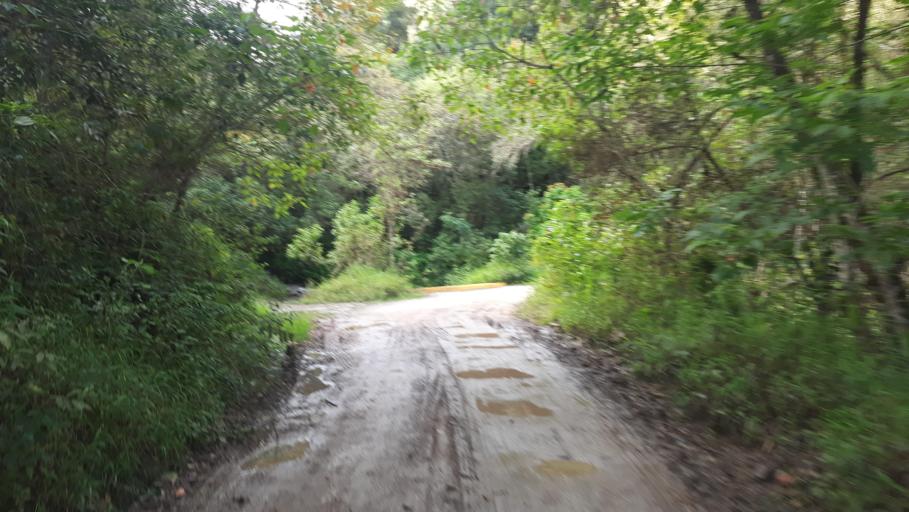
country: CO
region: Cundinamarca
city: Tenza
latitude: 5.1037
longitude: -73.4250
